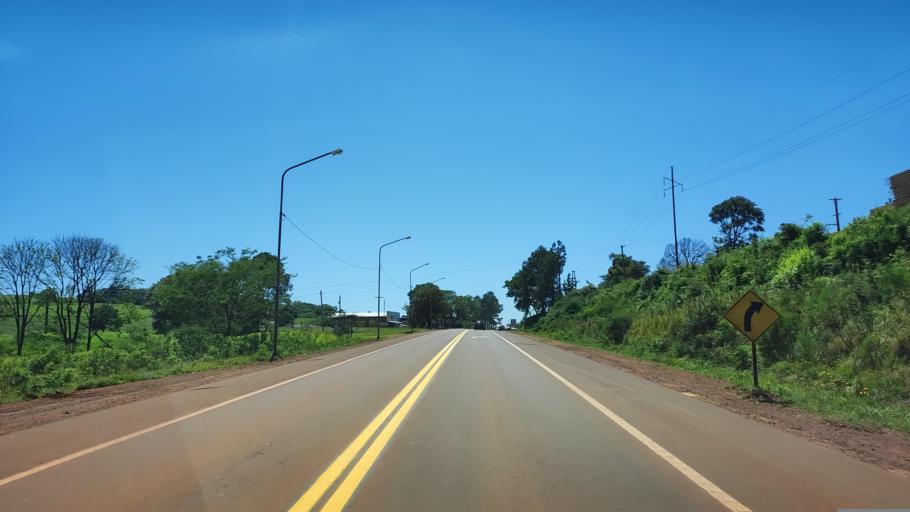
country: AR
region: Misiones
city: Aristobulo del Valle
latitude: -27.0835
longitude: -54.8176
